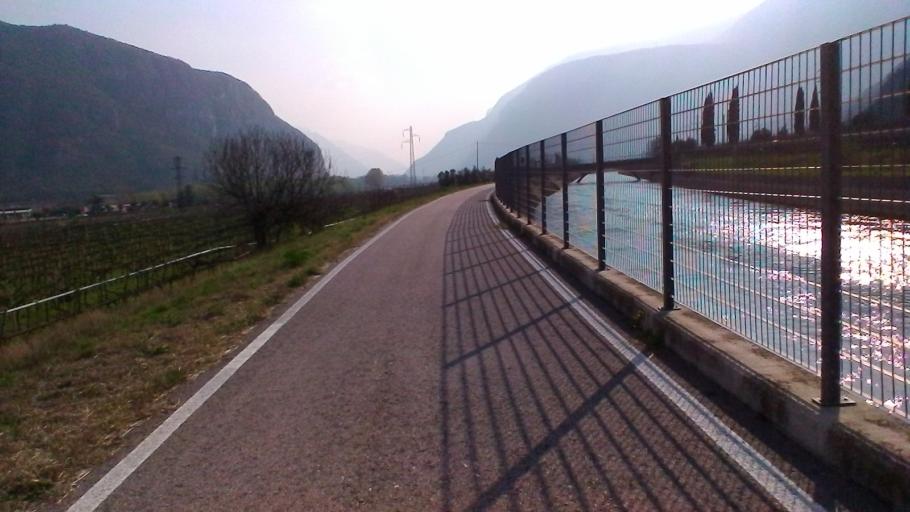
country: IT
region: Trentino-Alto Adige
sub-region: Provincia di Trento
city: Avio
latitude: 45.6988
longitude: 10.9165
